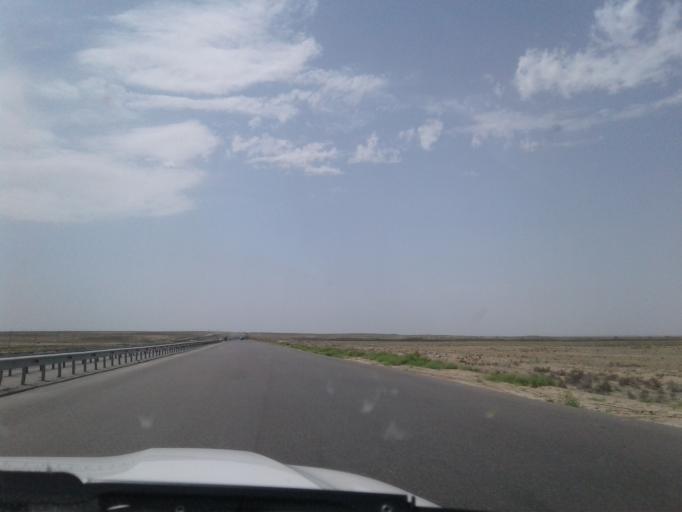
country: TM
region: Ahal
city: Kaka
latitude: 37.3265
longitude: 59.7257
